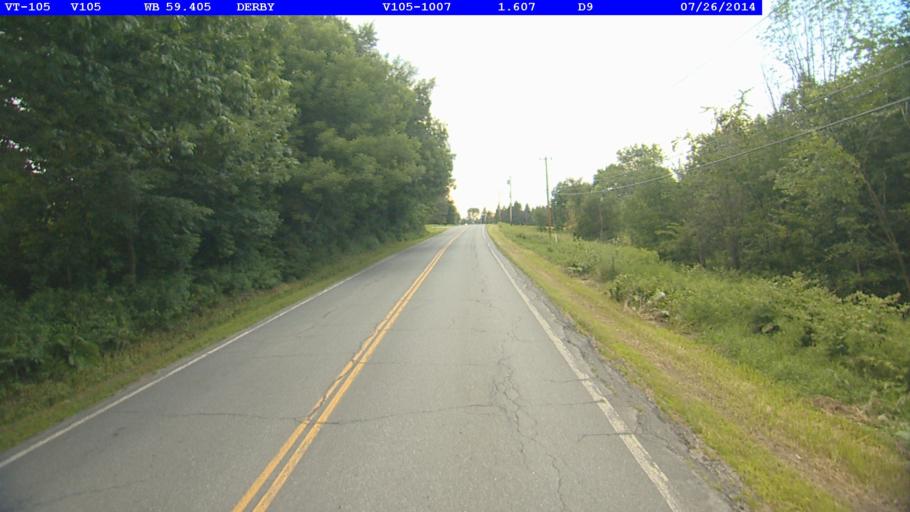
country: US
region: Vermont
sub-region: Orleans County
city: Newport
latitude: 44.9356
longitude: -72.1219
